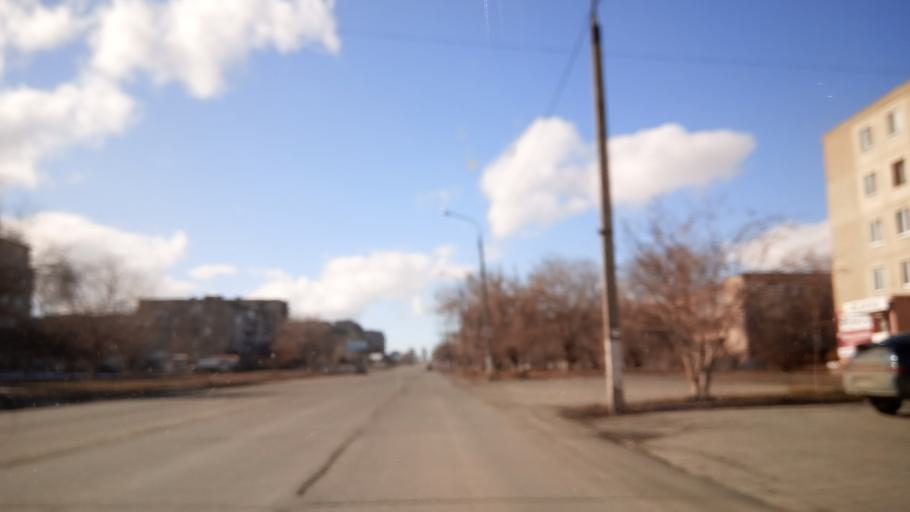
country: RU
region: Orenburg
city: Novotroitsk
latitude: 51.1839
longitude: 58.2827
